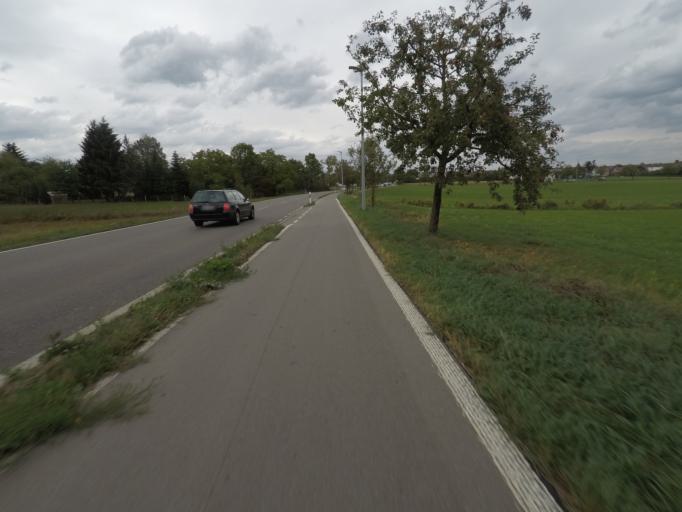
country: DE
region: Baden-Wuerttemberg
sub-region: Regierungsbezirk Stuttgart
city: Leinfelden-Echterdingen
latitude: 48.6782
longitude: 9.1671
